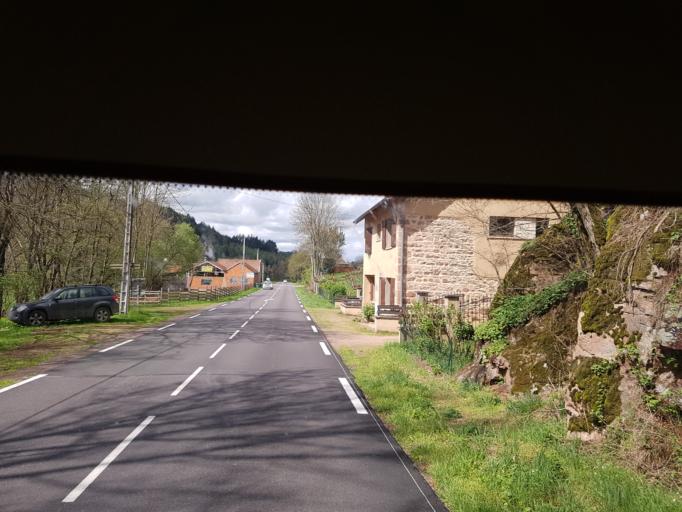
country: FR
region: Bourgogne
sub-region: Departement de Saone-et-Loire
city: La Clayette
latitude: 46.2808
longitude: 4.3686
